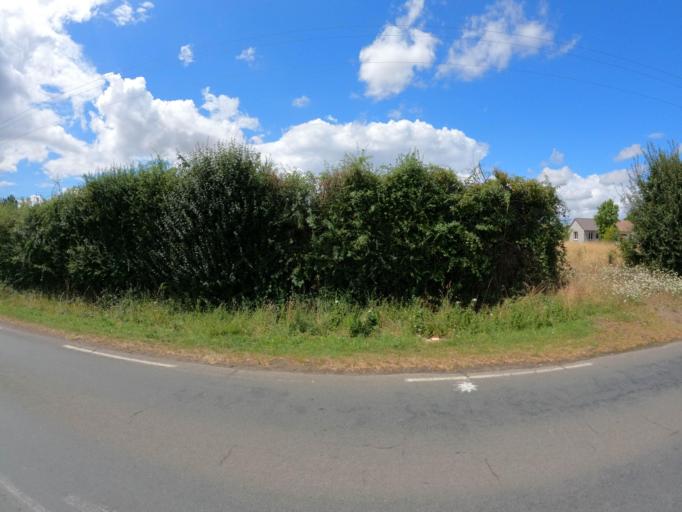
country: FR
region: Pays de la Loire
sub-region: Departement de la Sarthe
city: Juigne-sur-Sarthe
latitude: 47.9157
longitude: -0.2689
